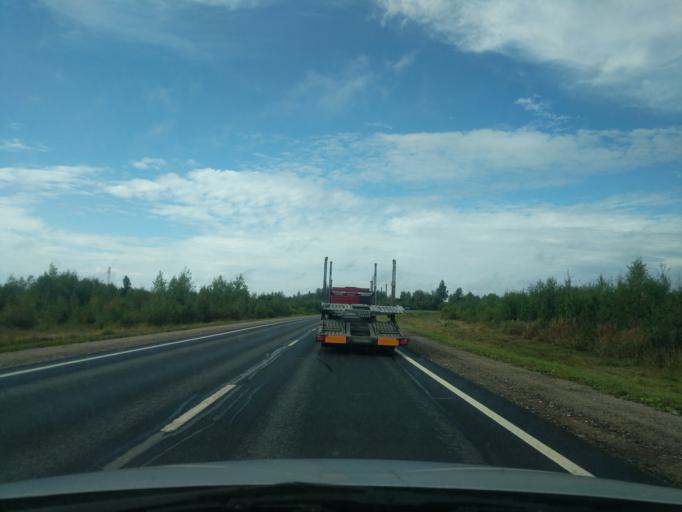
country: RU
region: Kostroma
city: Sudislavl'
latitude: 57.8219
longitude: 41.9044
